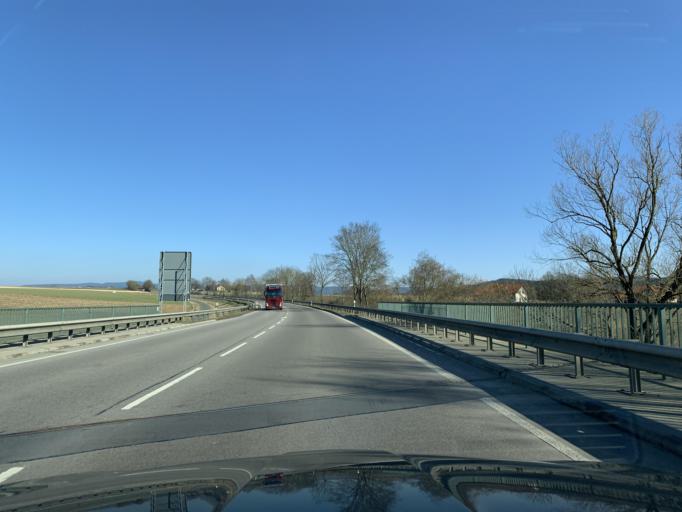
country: DE
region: Bavaria
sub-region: Upper Palatinate
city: Roetz
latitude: 49.3424
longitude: 12.5417
